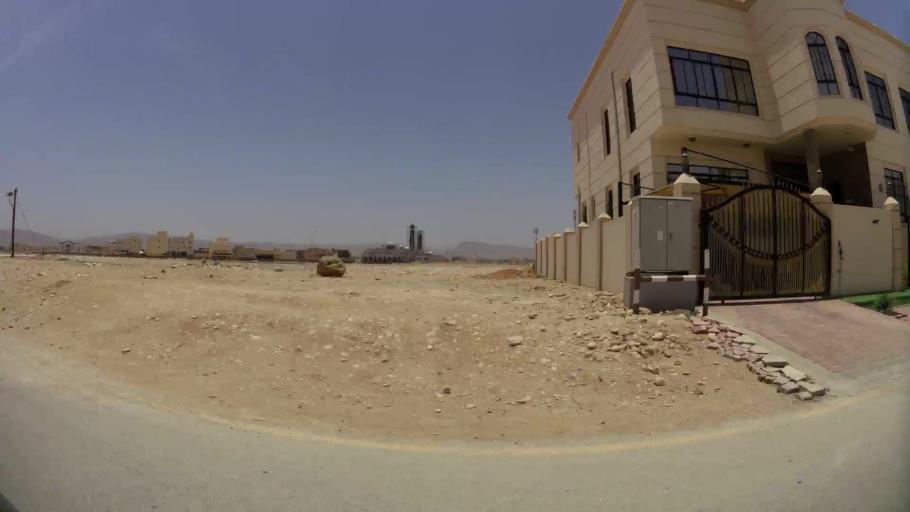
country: OM
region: Zufar
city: Salalah
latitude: 17.0828
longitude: 54.1610
